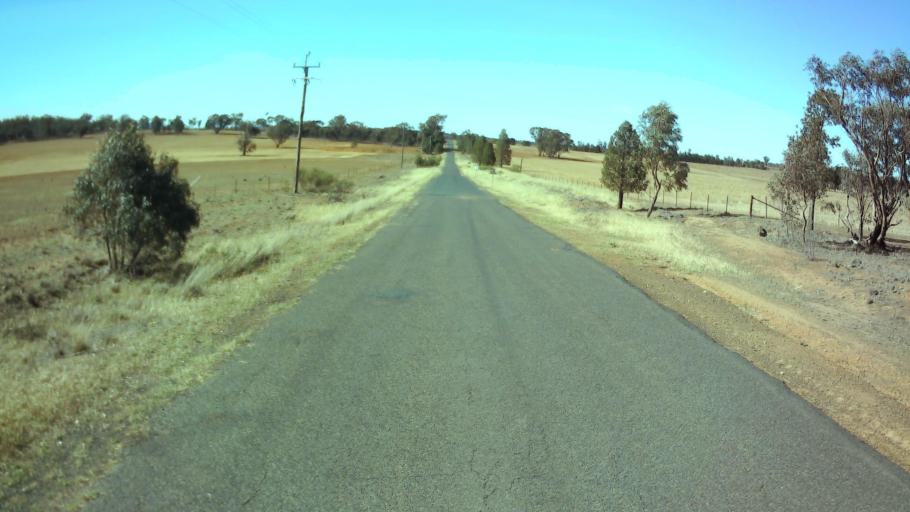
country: AU
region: New South Wales
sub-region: Weddin
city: Grenfell
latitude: -33.7624
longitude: 147.8292
